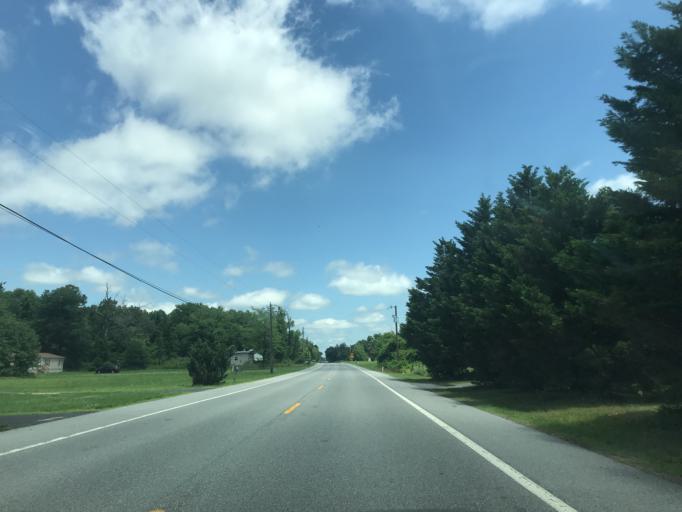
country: US
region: Maryland
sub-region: Caroline County
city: Federalsburg
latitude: 38.7062
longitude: -75.7510
